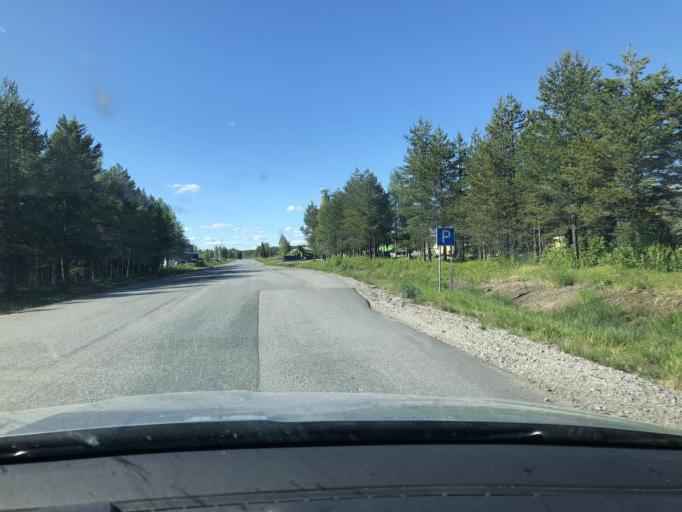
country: SE
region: Norrbotten
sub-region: Kalix Kommun
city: Kalix
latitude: 65.8472
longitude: 23.1984
